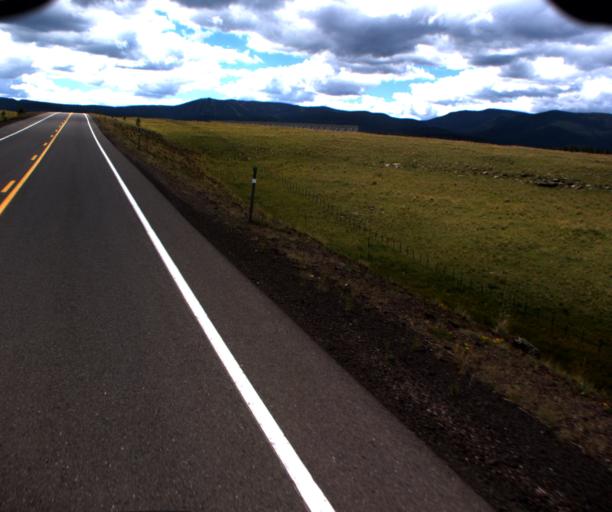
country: US
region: Arizona
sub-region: Apache County
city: Eagar
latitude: 34.0291
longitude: -109.5835
